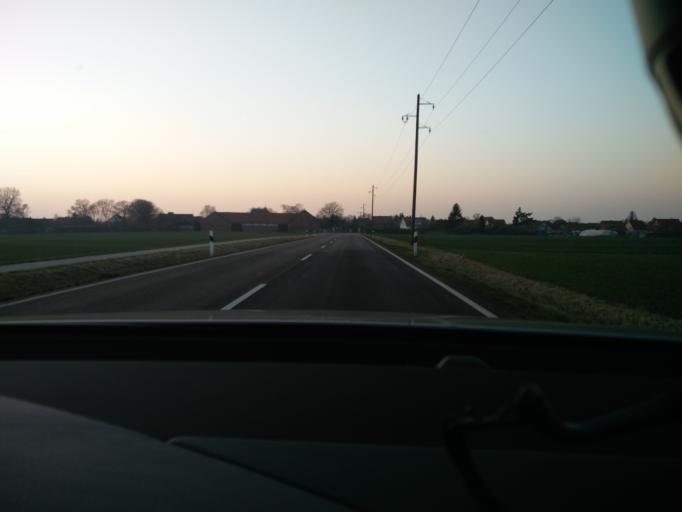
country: DE
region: Lower Saxony
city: Hohenhameln
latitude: 52.3066
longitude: 10.0558
